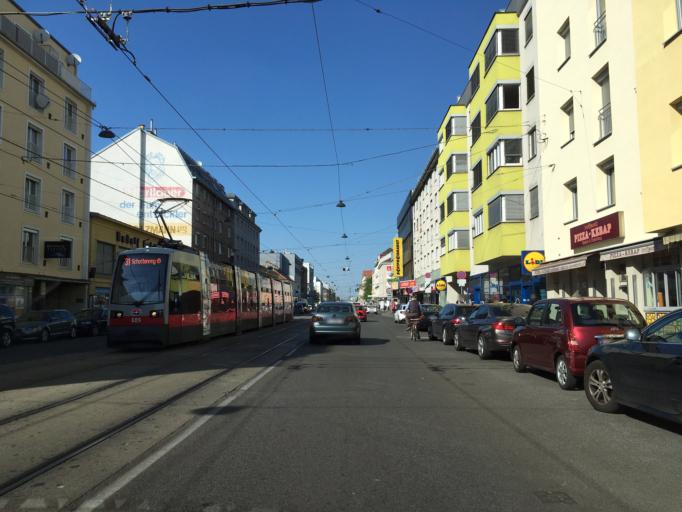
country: AT
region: Vienna
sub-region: Wien Stadt
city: Vienna
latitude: 48.2587
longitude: 16.3984
